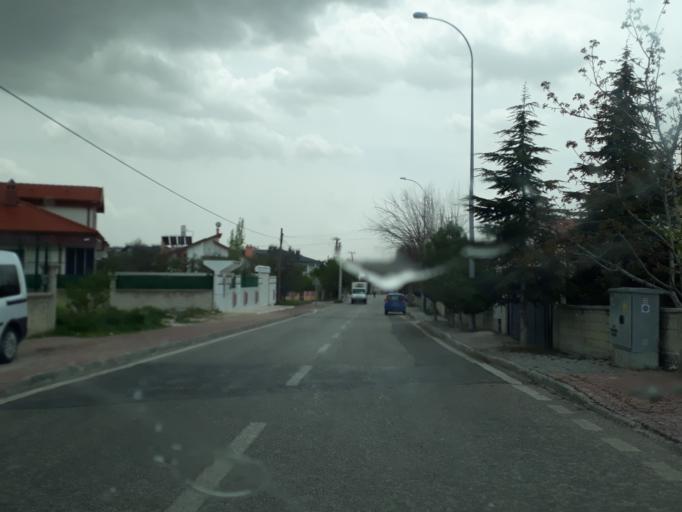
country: TR
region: Konya
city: Sille
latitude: 37.9190
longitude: 32.4636
